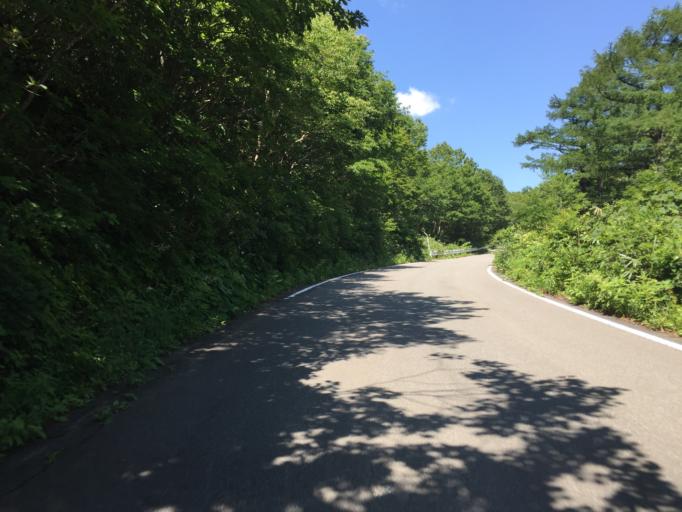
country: JP
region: Fukushima
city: Nihommatsu
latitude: 37.6554
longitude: 140.2954
